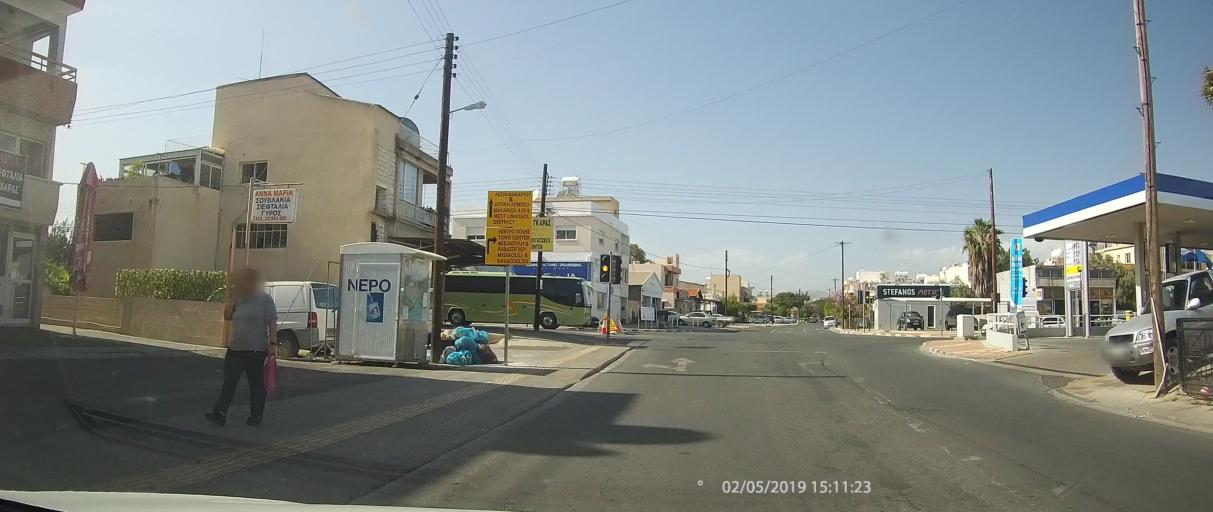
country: CY
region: Limassol
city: Limassol
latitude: 34.6733
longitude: 33.0218
